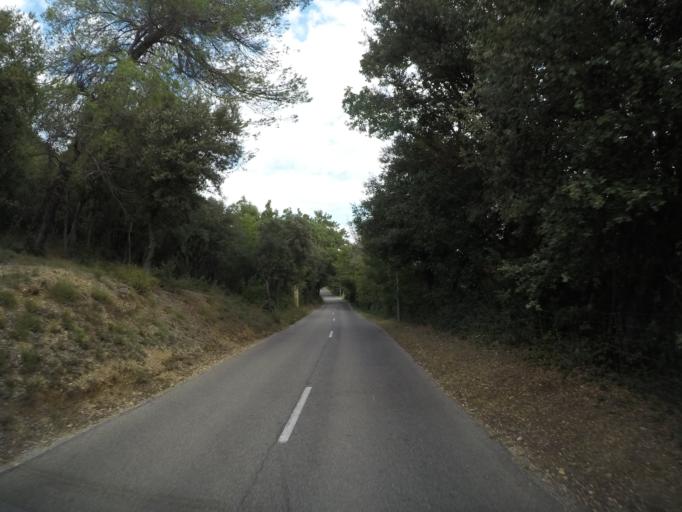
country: FR
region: Provence-Alpes-Cote d'Azur
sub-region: Departement des Alpes-de-Haute-Provence
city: Greoux-les-Bains
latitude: 43.7839
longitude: 5.9127
